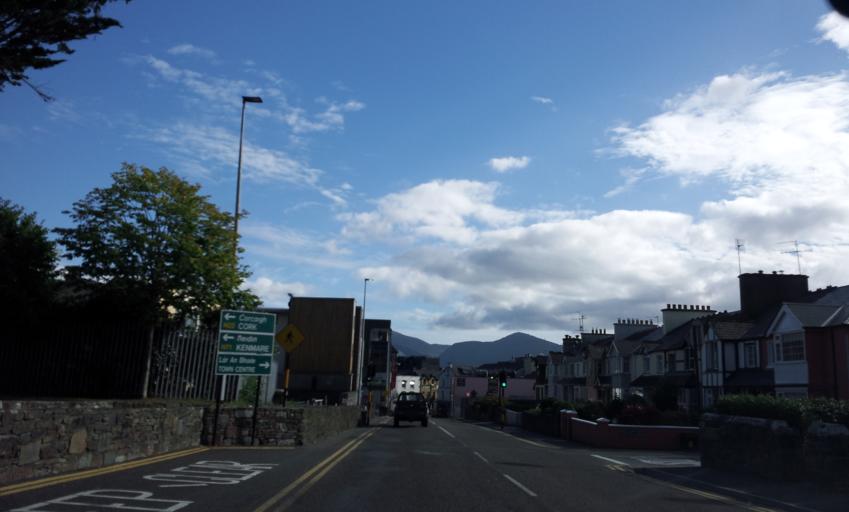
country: IE
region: Munster
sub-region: Ciarrai
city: Cill Airne
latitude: 52.0614
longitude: -9.5061
